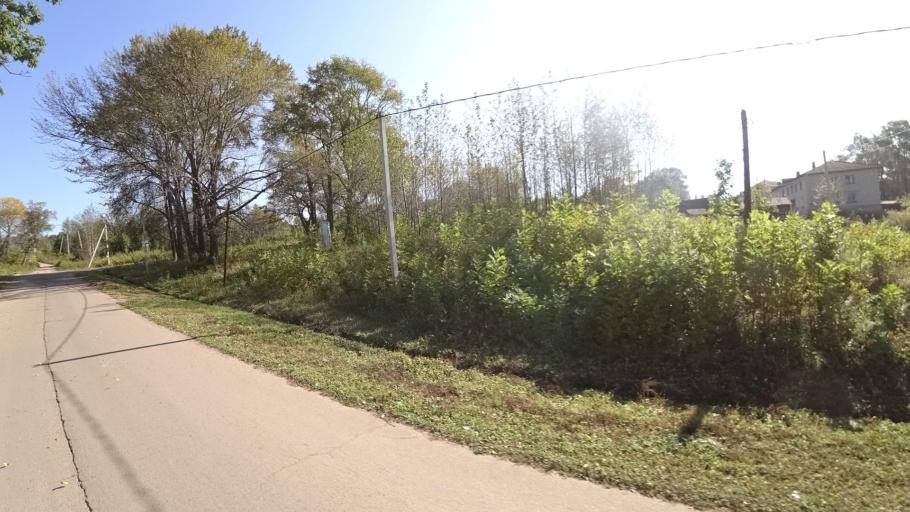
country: RU
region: Jewish Autonomous Oblast
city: Bira
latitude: 49.0038
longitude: 132.4657
